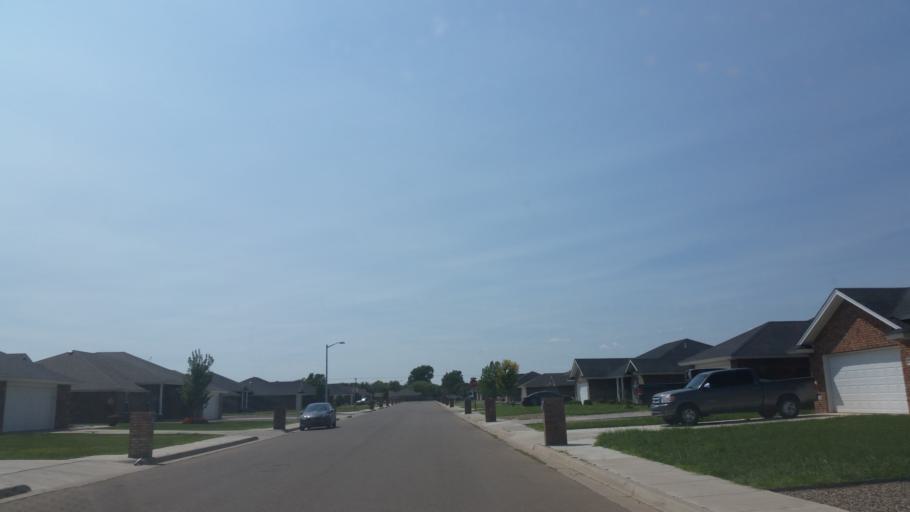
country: US
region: New Mexico
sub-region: Curry County
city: Clovis
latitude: 34.4443
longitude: -103.1752
